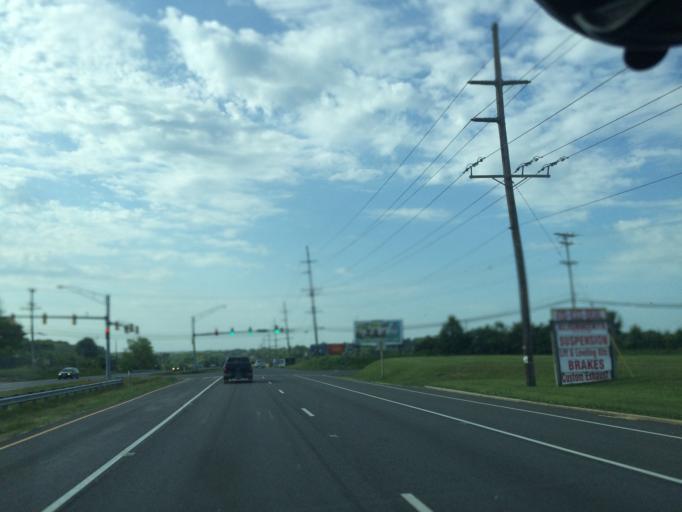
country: US
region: Maryland
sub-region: Carroll County
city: Westminster
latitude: 39.5396
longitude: -76.9316
